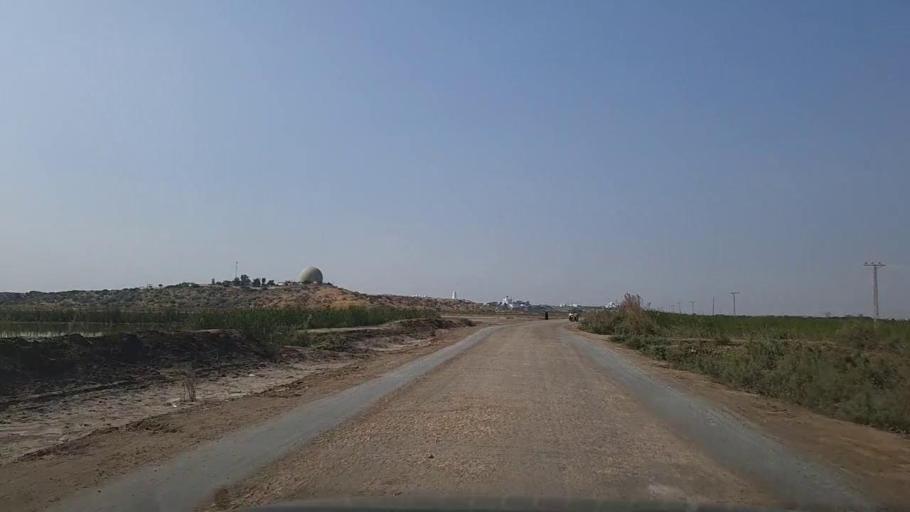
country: PK
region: Sindh
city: Chuhar Jamali
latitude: 24.5510
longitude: 67.8935
